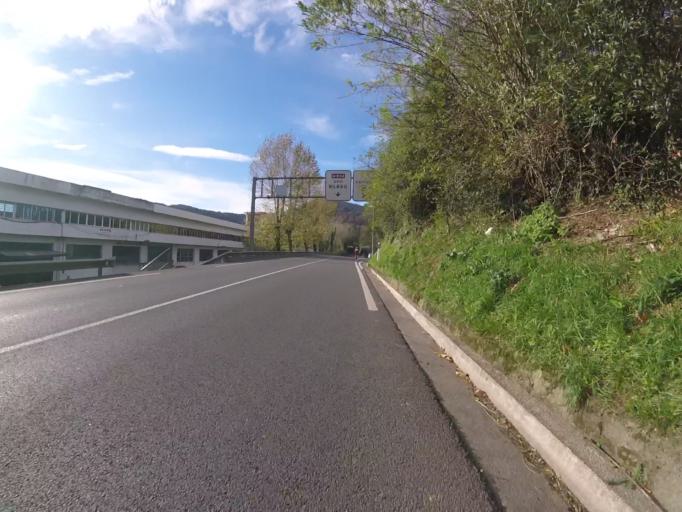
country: ES
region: Basque Country
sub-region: Provincia de Guipuzcoa
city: Usurbil
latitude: 43.2693
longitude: -2.0467
